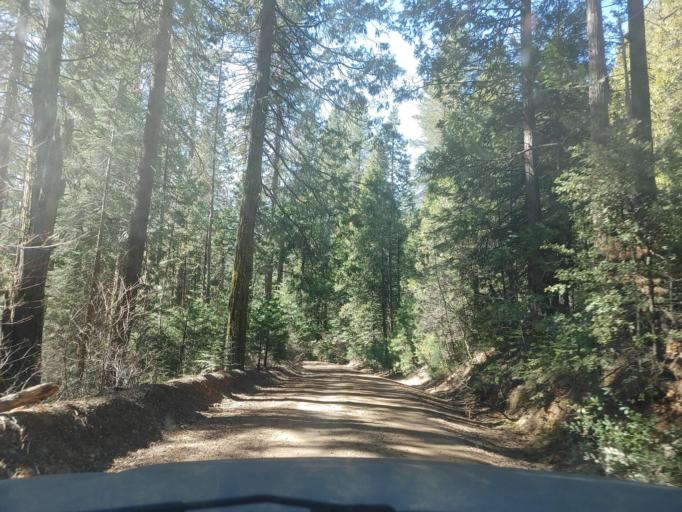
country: US
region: California
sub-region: Madera County
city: Ahwahnee
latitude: 37.4416
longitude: -119.6675
